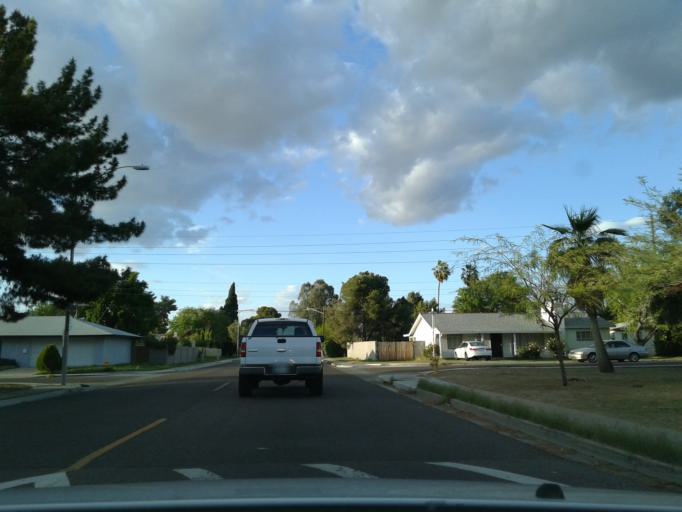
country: US
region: Arizona
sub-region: Maricopa County
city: Glendale
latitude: 33.5269
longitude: -112.1040
